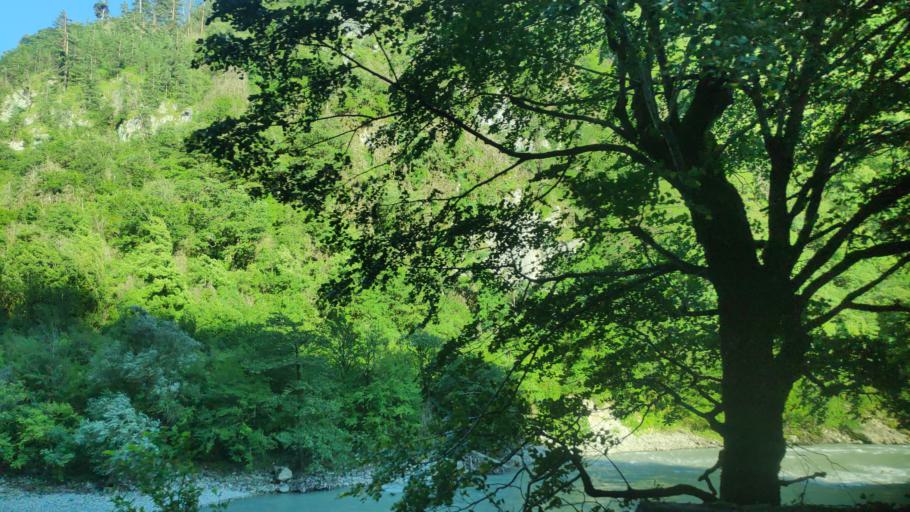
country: GE
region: Abkhazia
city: Gagra
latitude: 43.3671
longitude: 40.4565
